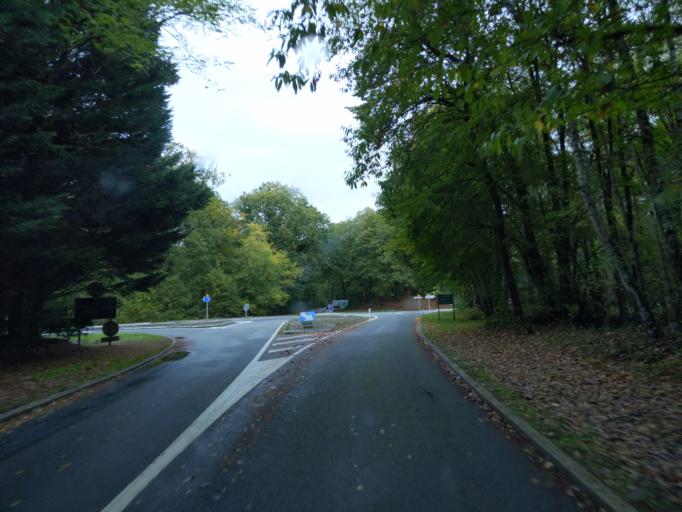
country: FR
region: Ile-de-France
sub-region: Departement des Yvelines
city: Bullion
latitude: 48.5930
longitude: 1.9923
